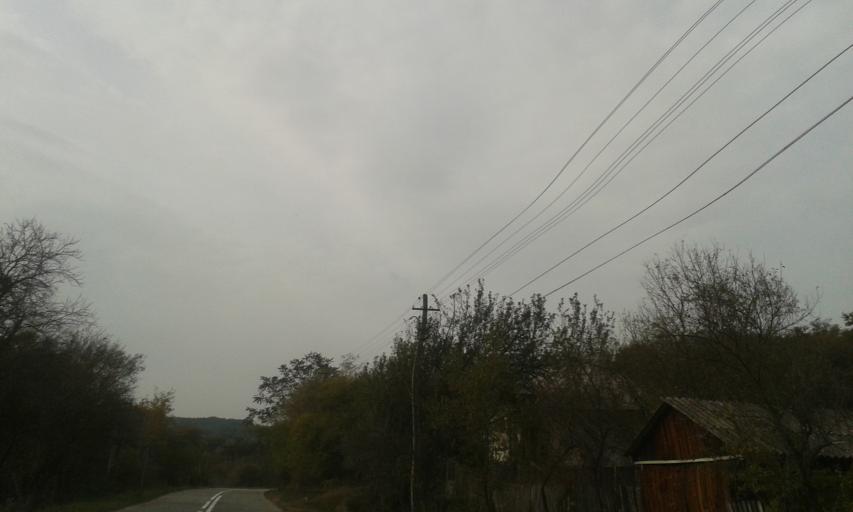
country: RO
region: Valcea
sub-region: Comuna Gradistea
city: Gradistea
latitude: 44.9035
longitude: 23.8003
